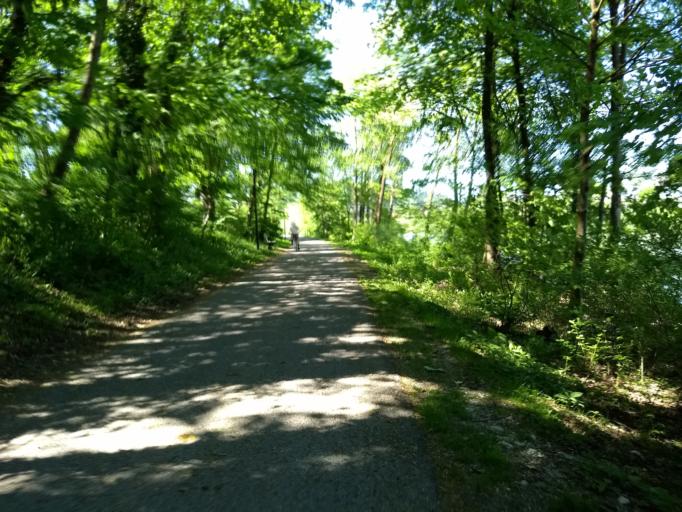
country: AT
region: Salzburg
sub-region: Salzburg Stadt
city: Salzburg
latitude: 47.7846
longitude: 13.0745
